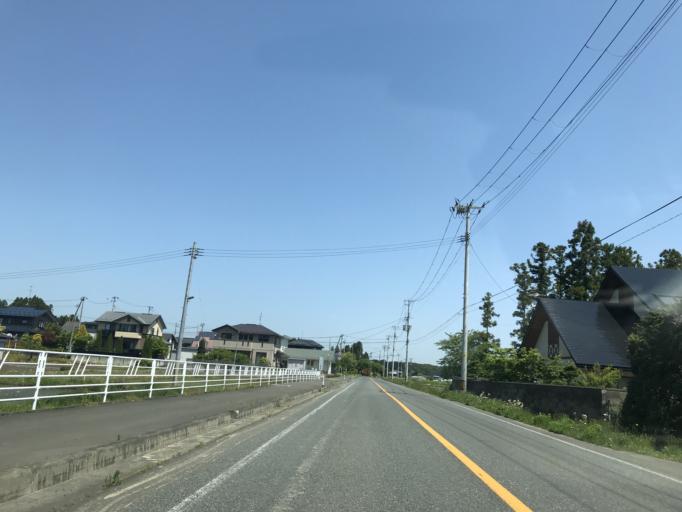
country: JP
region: Iwate
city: Kitakami
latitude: 39.2209
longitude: 141.0658
